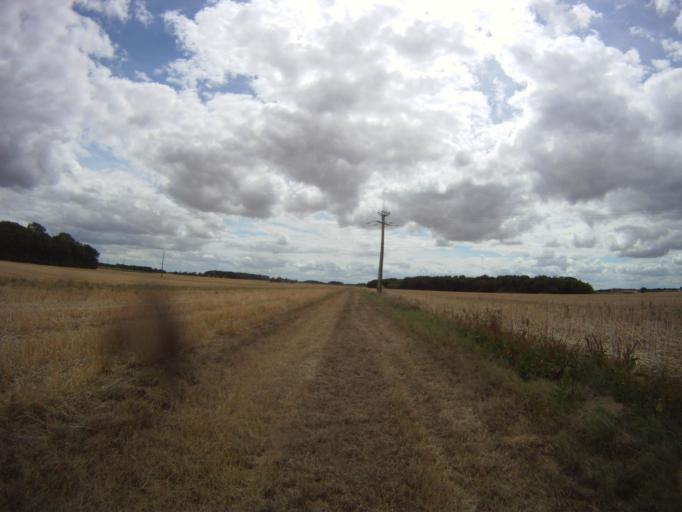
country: FR
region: Centre
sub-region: Departement du Loir-et-Cher
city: Montoire-sur-le-Loir
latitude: 47.6933
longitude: 0.8114
